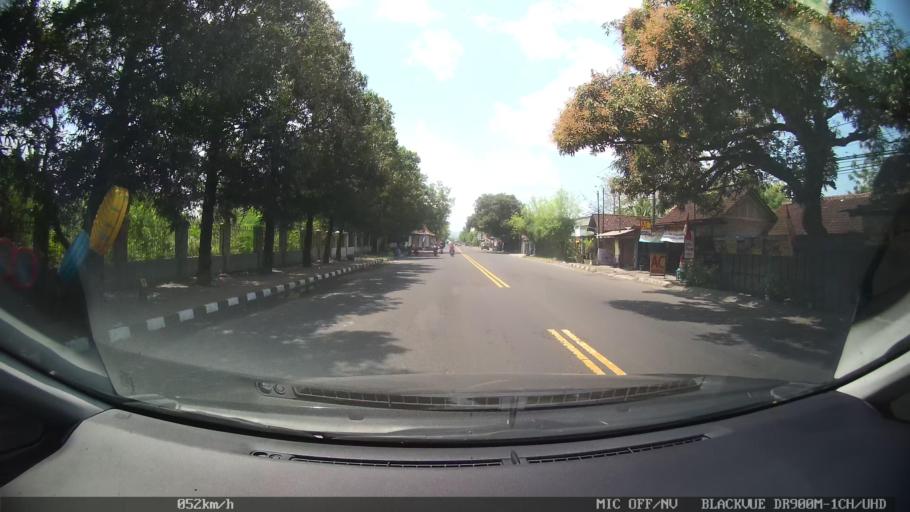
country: ID
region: Daerah Istimewa Yogyakarta
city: Bantul
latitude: -7.9057
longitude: 110.3176
